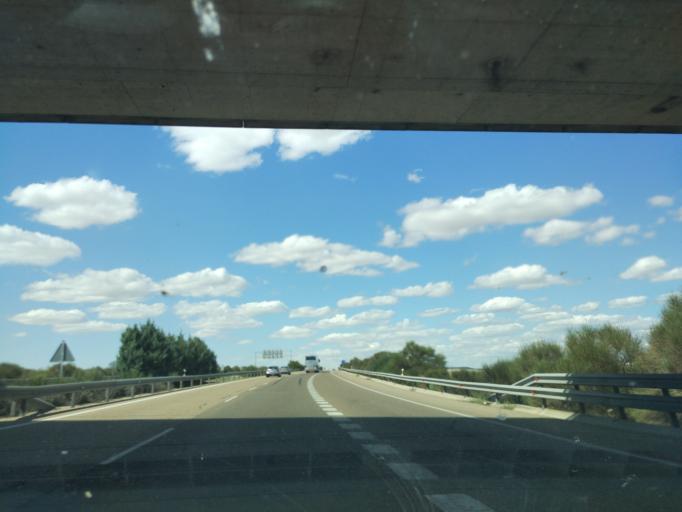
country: ES
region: Castille and Leon
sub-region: Provincia de Valladolid
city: Medina del Campo
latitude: 41.2943
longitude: -4.9013
